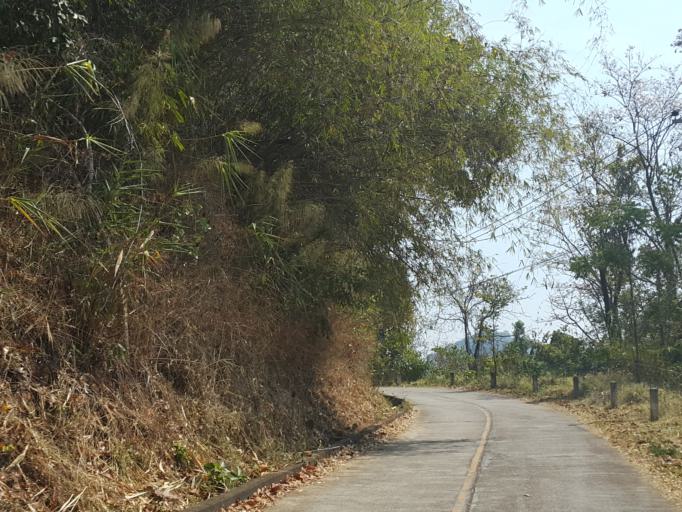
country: TH
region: Lampang
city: Mueang Pan
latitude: 18.8278
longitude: 99.3934
